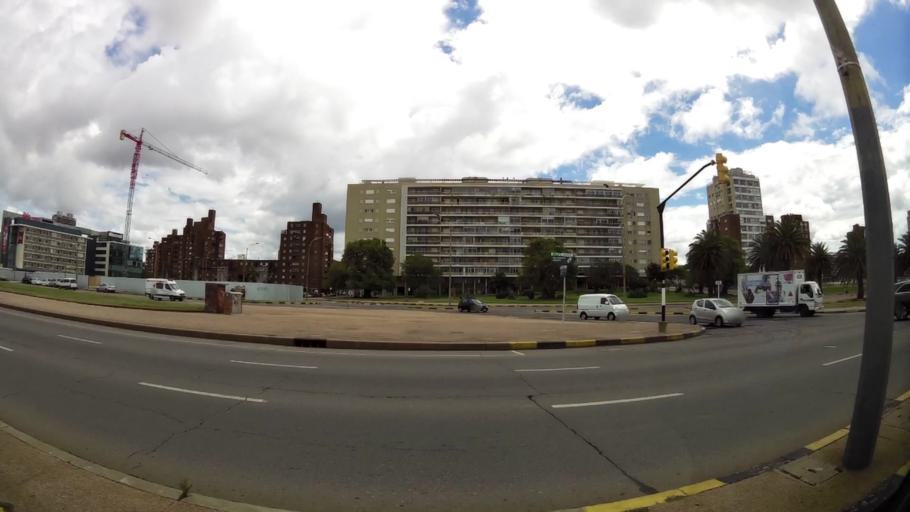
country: UY
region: Montevideo
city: Montevideo
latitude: -34.9149
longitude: -56.1807
